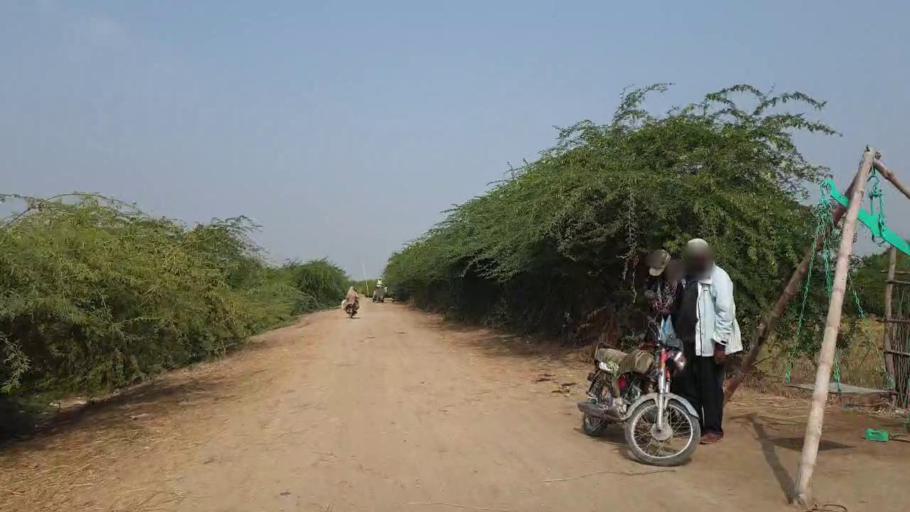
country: PK
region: Sindh
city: Kario
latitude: 24.7563
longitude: 68.5583
